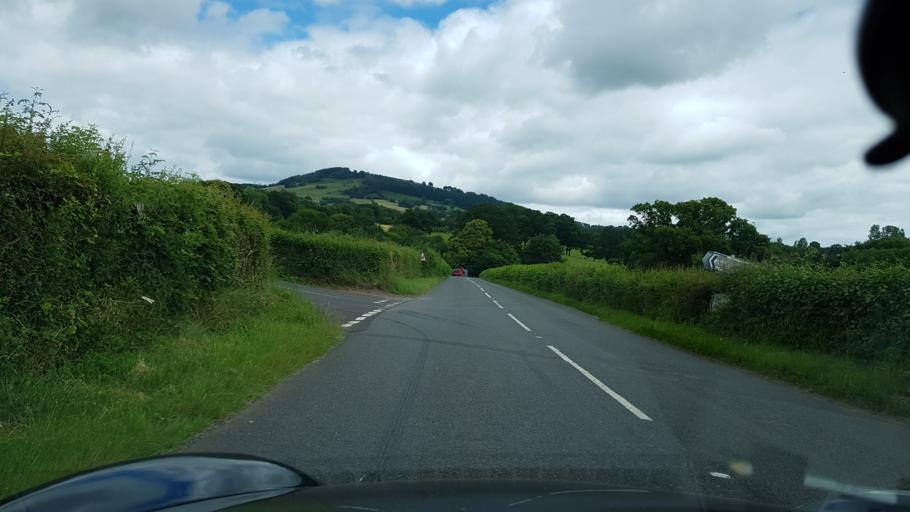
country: GB
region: Wales
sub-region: Monmouthshire
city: Grosmont
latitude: 51.8640
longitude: -2.8843
